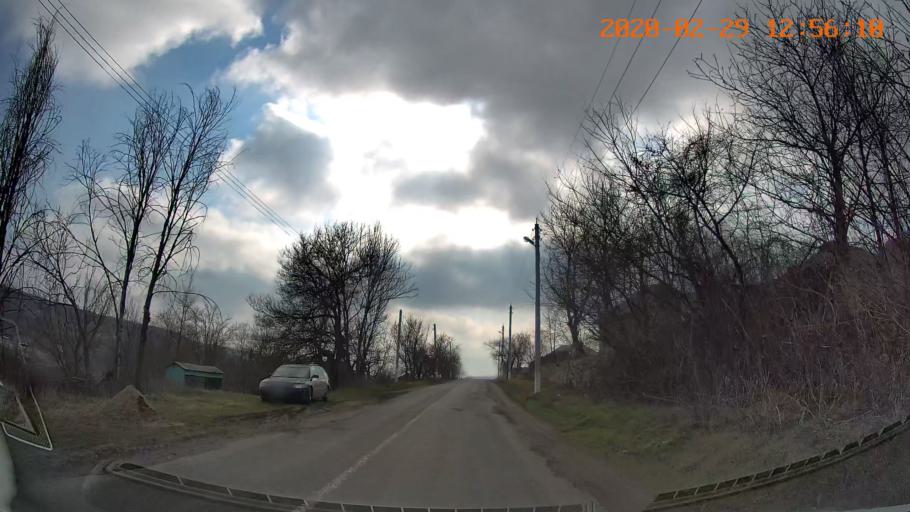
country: MD
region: Telenesti
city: Camenca
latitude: 48.0893
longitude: 28.7231
